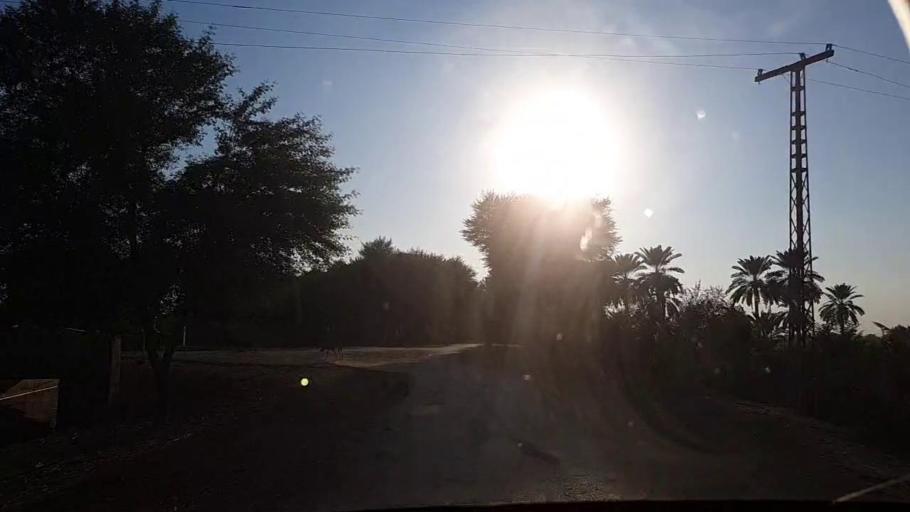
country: PK
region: Sindh
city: Sobhadero
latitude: 27.4117
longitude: 68.3953
